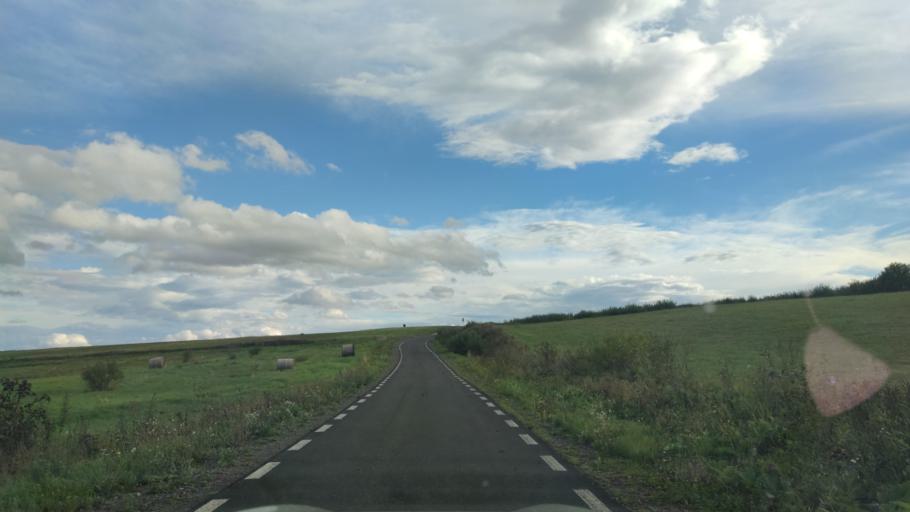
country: RO
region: Harghita
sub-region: Comuna Remetea
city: Remetea
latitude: 46.8073
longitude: 25.4233
